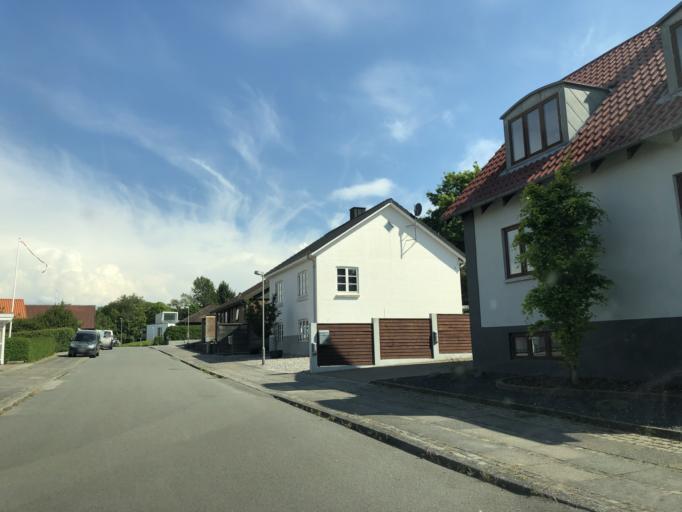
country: DK
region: Central Jutland
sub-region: Holstebro Kommune
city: Holstebro
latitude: 56.3559
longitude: 8.6056
